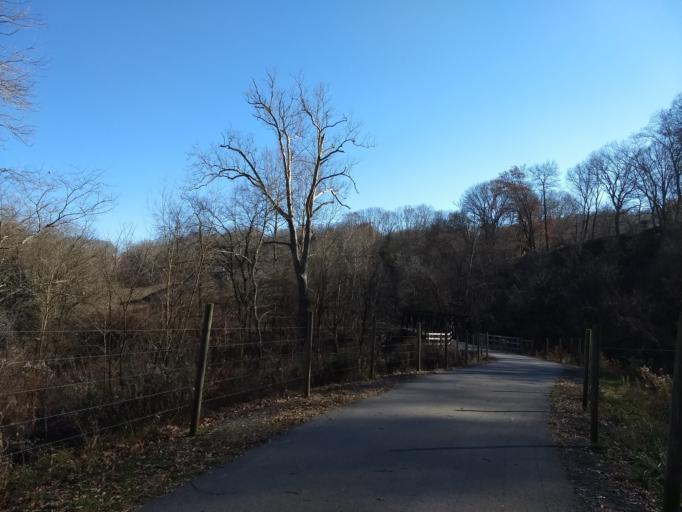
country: US
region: Pennsylvania
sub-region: Allegheny County
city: South Park Township
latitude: 40.2814
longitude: -79.9853
